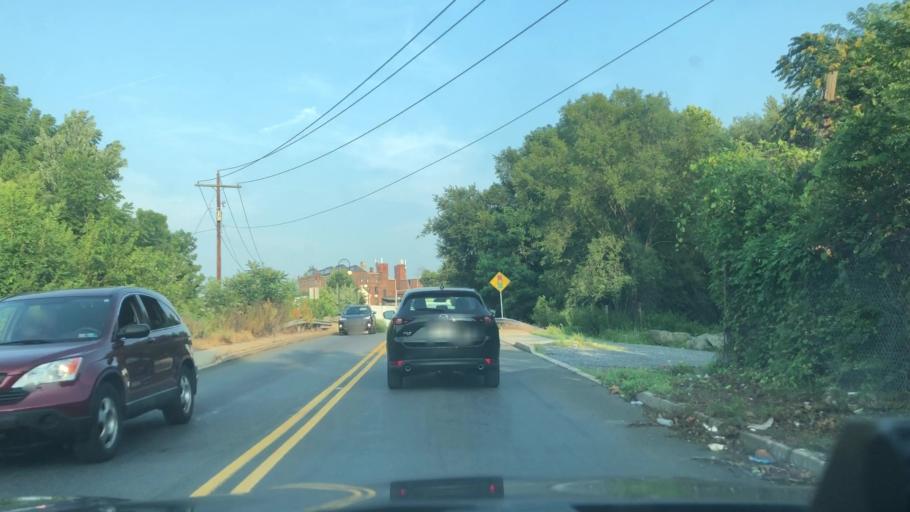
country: US
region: Pennsylvania
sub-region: Lehigh County
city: Fullerton
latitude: 40.6178
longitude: -75.4649
